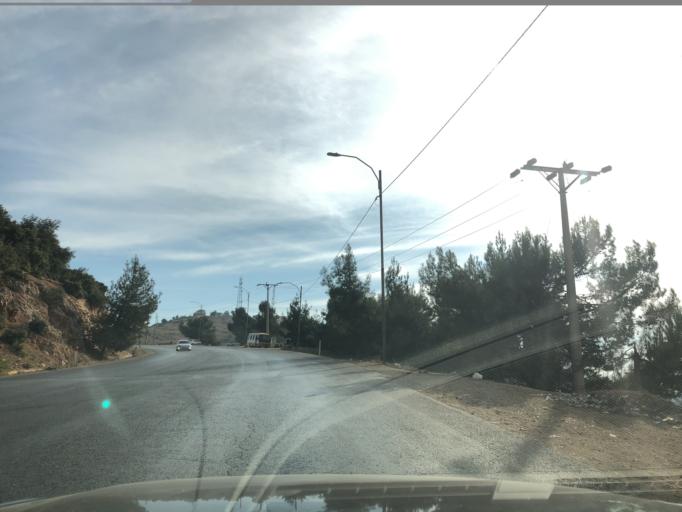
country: JO
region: Irbid
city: `Anjarah
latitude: 32.3065
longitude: 35.7760
